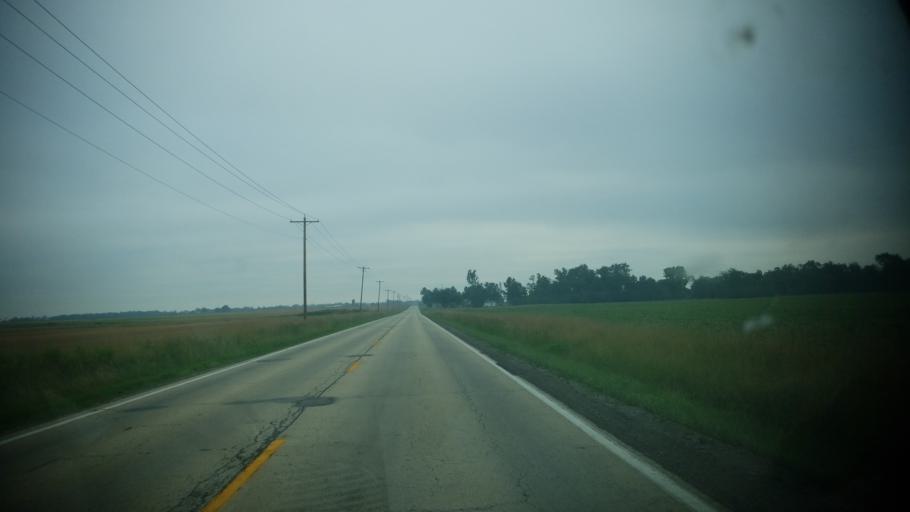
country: US
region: Illinois
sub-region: Clay County
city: Flora
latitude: 38.6517
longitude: -88.4384
